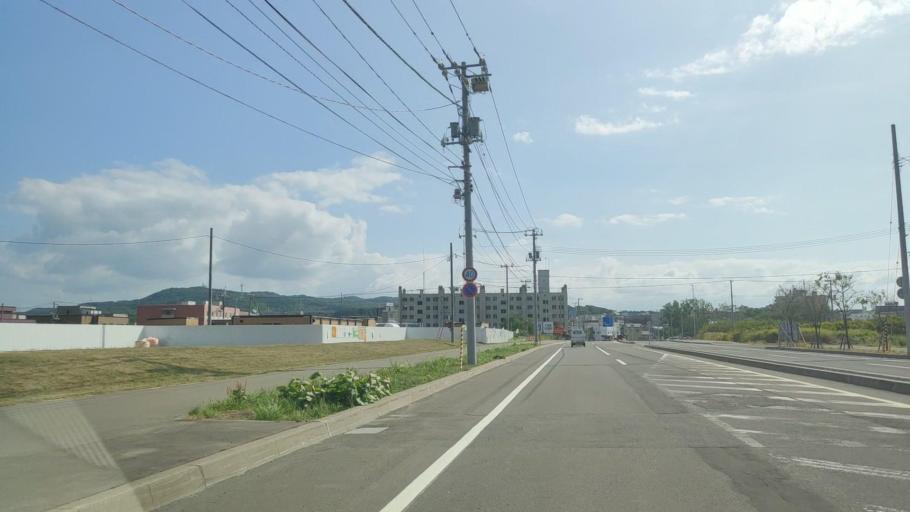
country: JP
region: Hokkaido
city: Rumoi
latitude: 43.9443
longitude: 141.6478
